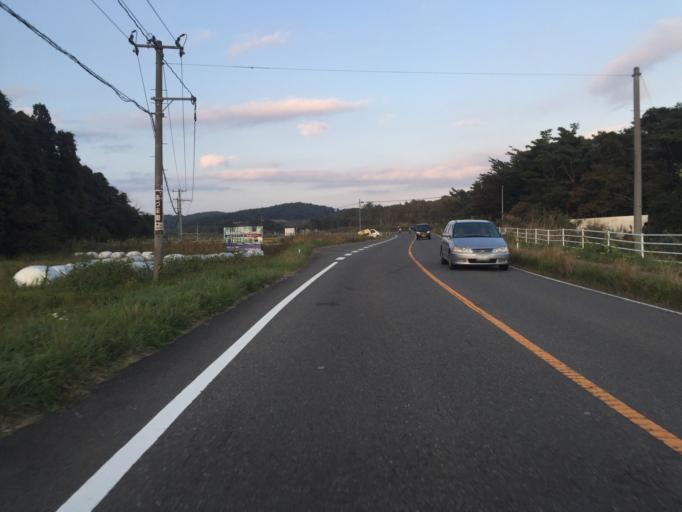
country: JP
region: Fukushima
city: Nihommatsu
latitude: 37.5883
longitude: 140.3535
